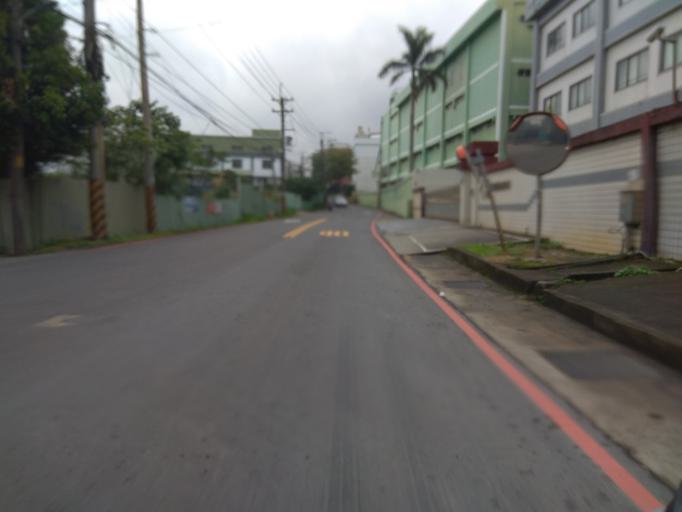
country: TW
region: Taiwan
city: Daxi
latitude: 24.9240
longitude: 121.1656
